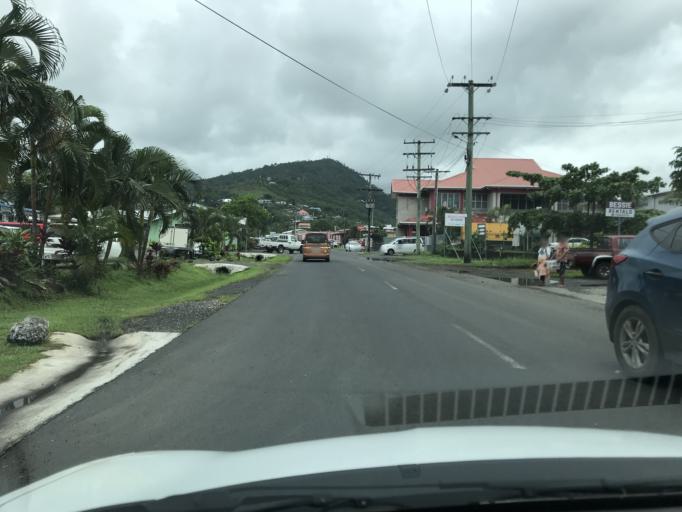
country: WS
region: Tuamasaga
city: Apia
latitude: -13.8325
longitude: -171.7679
